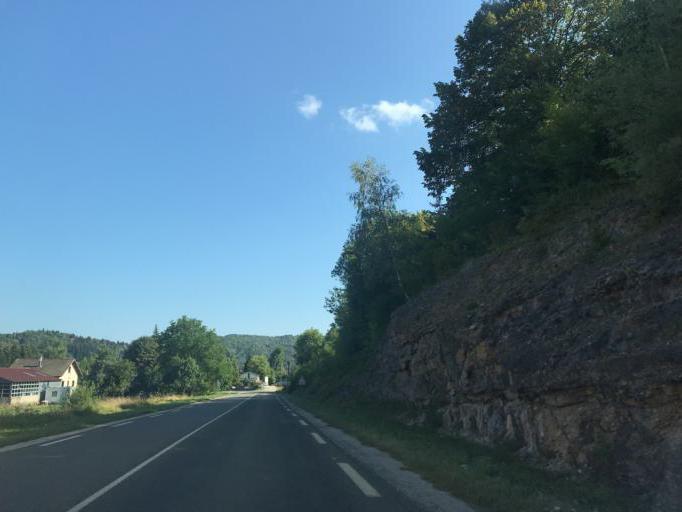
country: FR
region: Franche-Comte
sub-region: Departement du Jura
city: Moirans-en-Montagne
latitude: 46.4065
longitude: 5.7343
